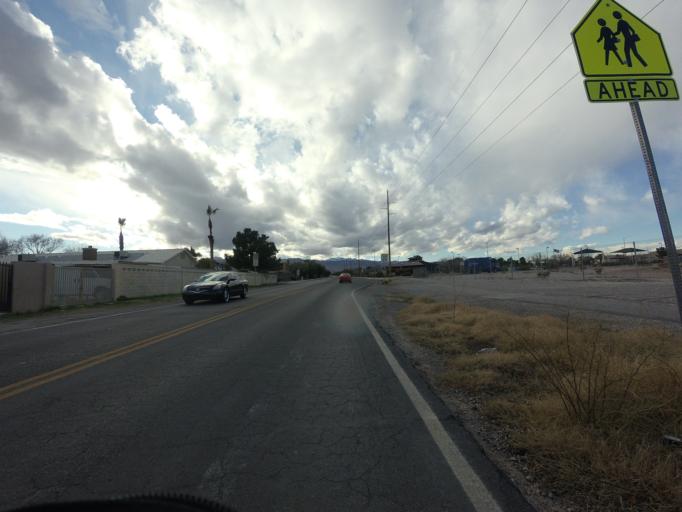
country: US
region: Nevada
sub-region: Clark County
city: Las Vegas
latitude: 36.2692
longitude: -115.2373
